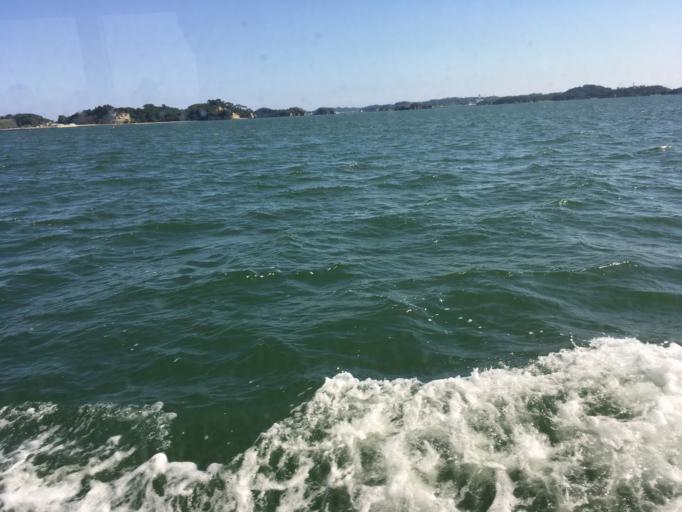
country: JP
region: Miyagi
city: Matsushima
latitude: 38.3486
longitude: 141.0820
